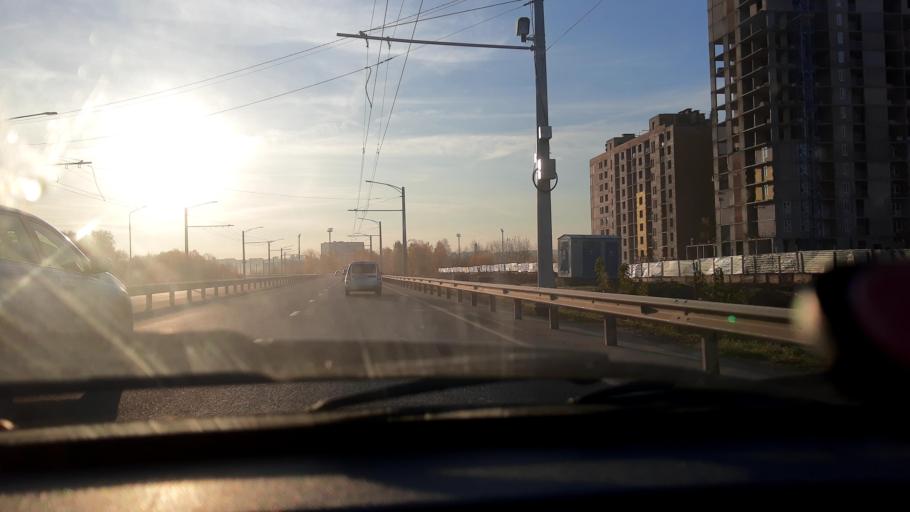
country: RU
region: Bashkortostan
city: Mikhaylovka
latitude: 54.7722
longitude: 55.9016
